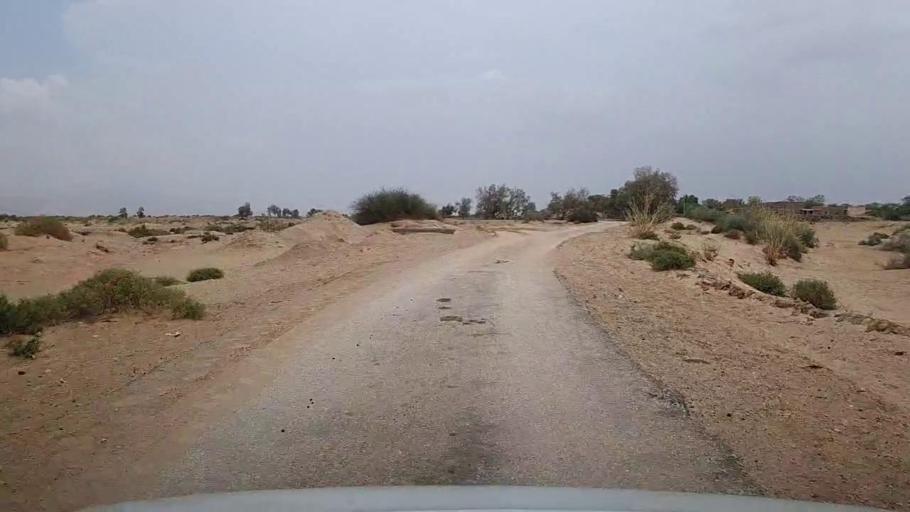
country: PK
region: Sindh
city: Sehwan
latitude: 26.3485
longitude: 67.7952
